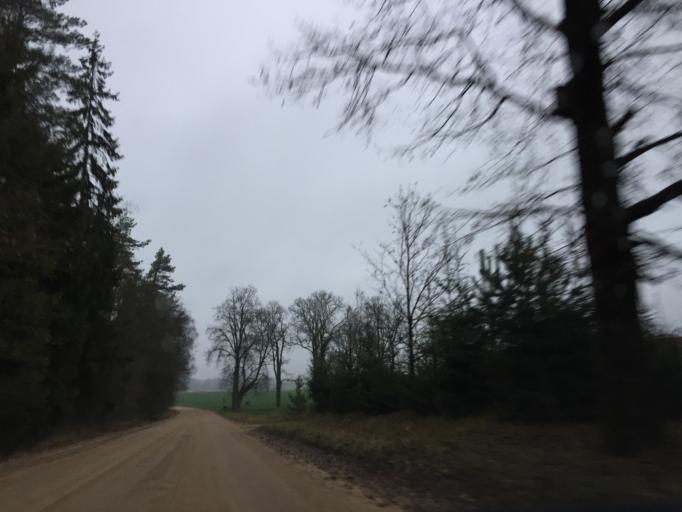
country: LV
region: Koceni
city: Koceni
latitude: 57.5390
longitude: 25.3325
